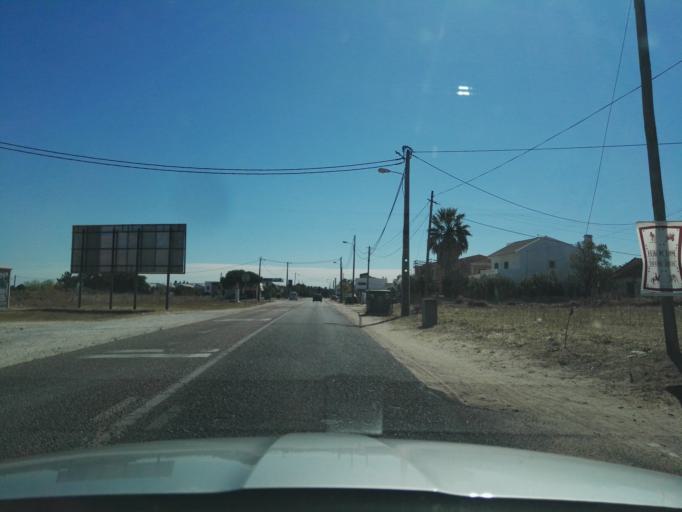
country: PT
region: Setubal
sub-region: Alcochete
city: Alcochete
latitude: 38.7550
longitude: -8.9491
